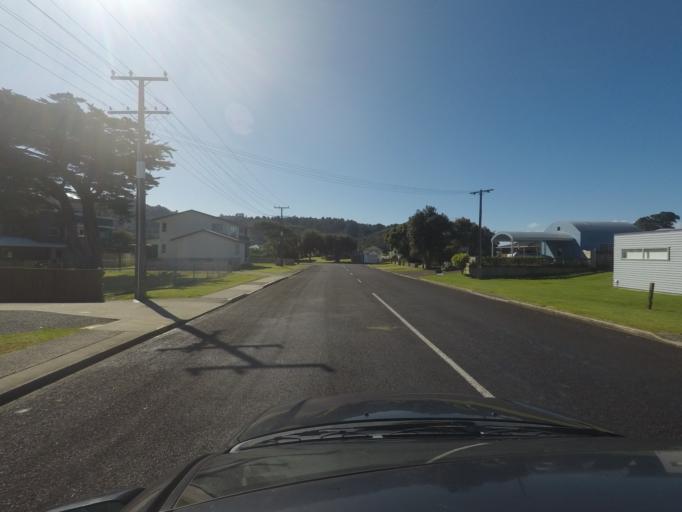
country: NZ
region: Bay of Plenty
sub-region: Western Bay of Plenty District
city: Waihi Beach
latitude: -37.4034
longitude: 175.9403
